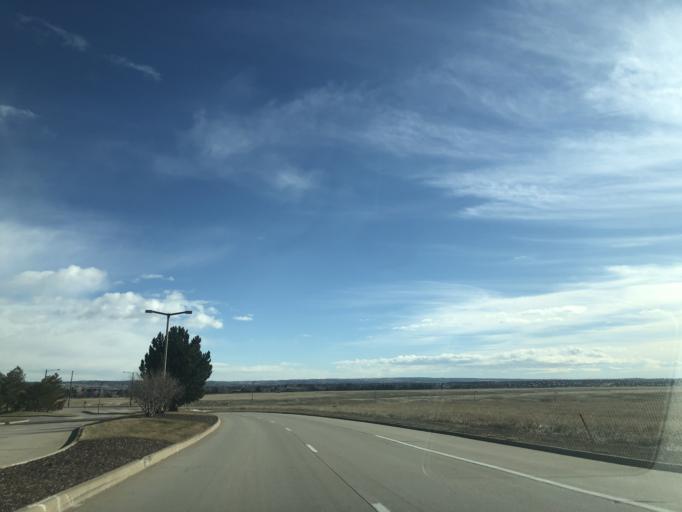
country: US
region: Colorado
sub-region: Douglas County
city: Meridian
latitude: 39.5472
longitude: -104.8422
